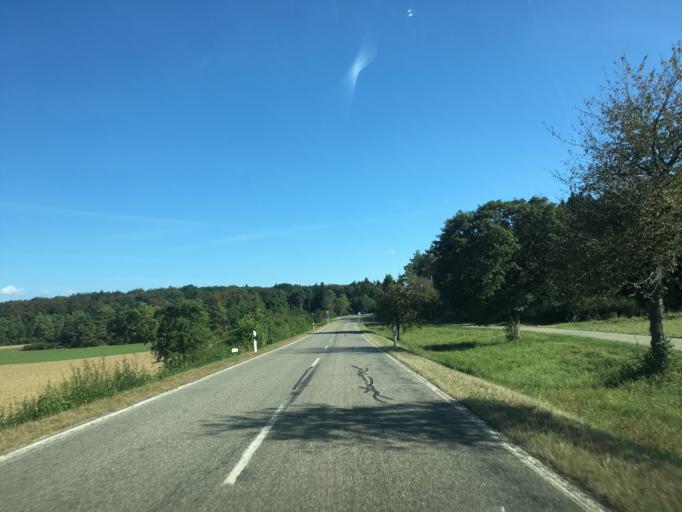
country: DE
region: Baden-Wuerttemberg
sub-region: Tuebingen Region
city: Hayingen
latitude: 48.2653
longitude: 9.4961
